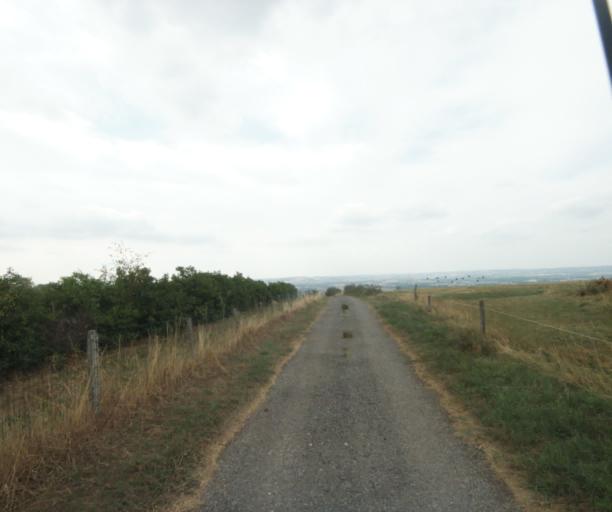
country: FR
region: Midi-Pyrenees
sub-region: Departement de la Haute-Garonne
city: Revel
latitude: 43.4408
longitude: 2.0157
